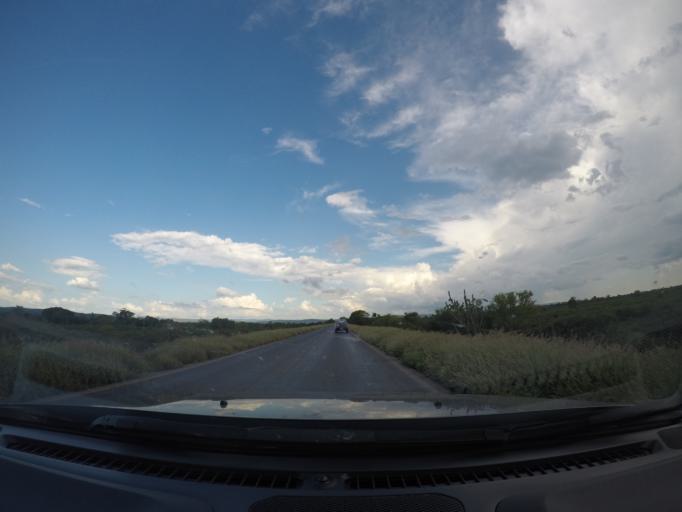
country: BR
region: Bahia
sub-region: Ibotirama
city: Ibotirama
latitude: -12.1546
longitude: -43.3072
